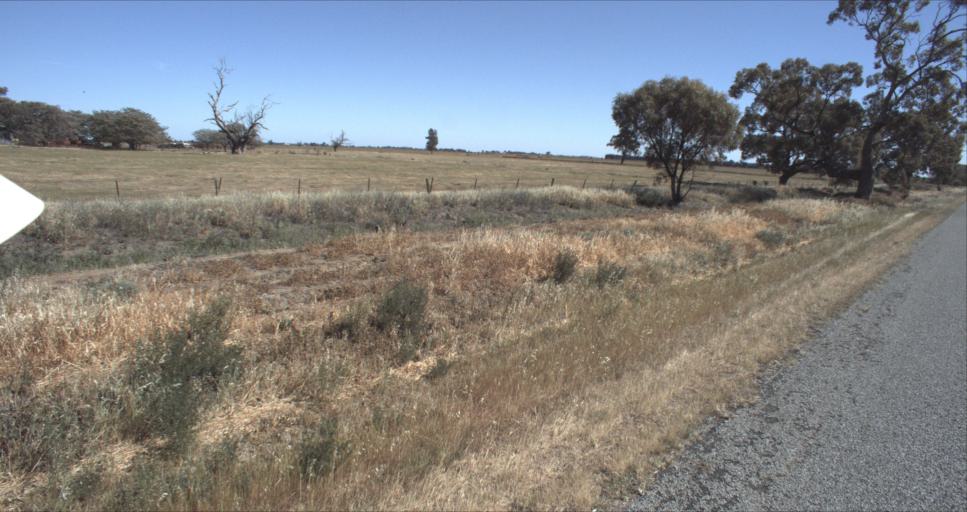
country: AU
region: New South Wales
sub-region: Leeton
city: Leeton
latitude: -34.5425
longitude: 146.3162
